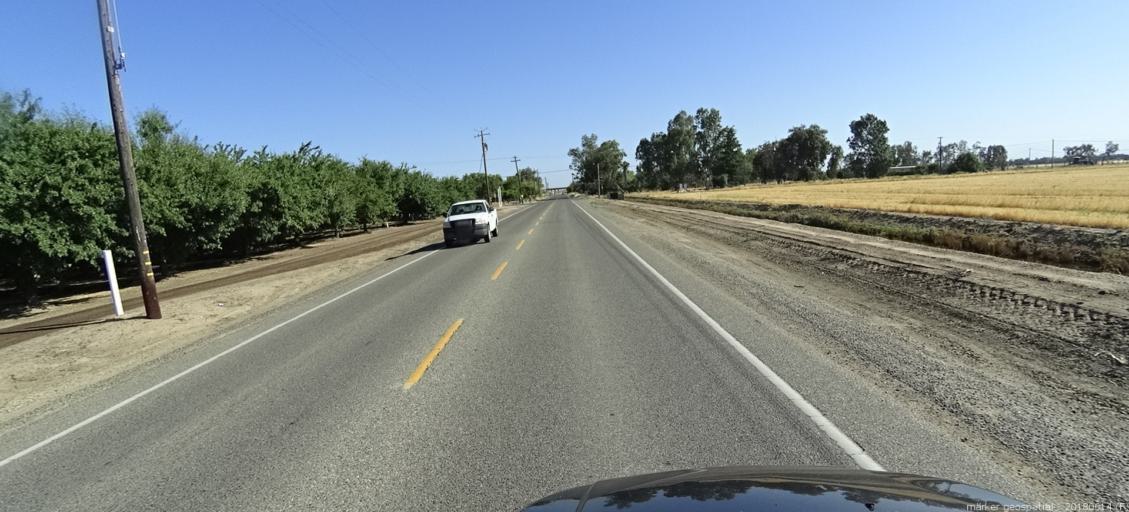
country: US
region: California
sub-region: Madera County
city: Madera Acres
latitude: 37.0097
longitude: -120.1287
